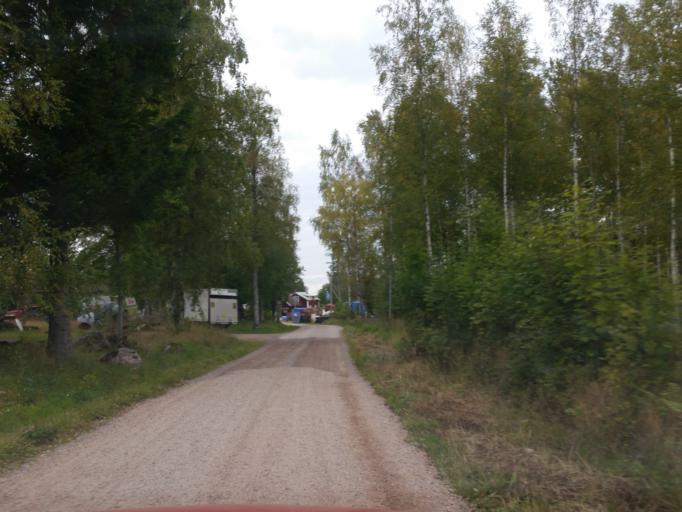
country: SE
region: Dalarna
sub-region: Leksand Municipality
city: Smedby
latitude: 60.6700
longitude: 15.1283
